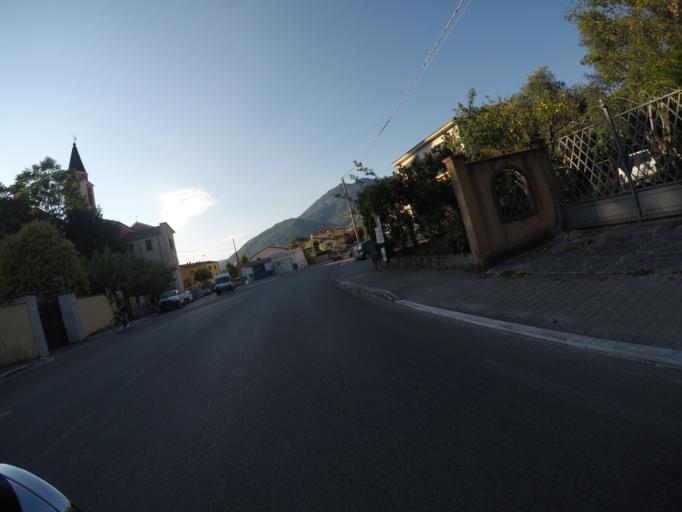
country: IT
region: Tuscany
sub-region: Provincia di Massa-Carrara
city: Massa
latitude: 44.0291
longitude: 10.1444
